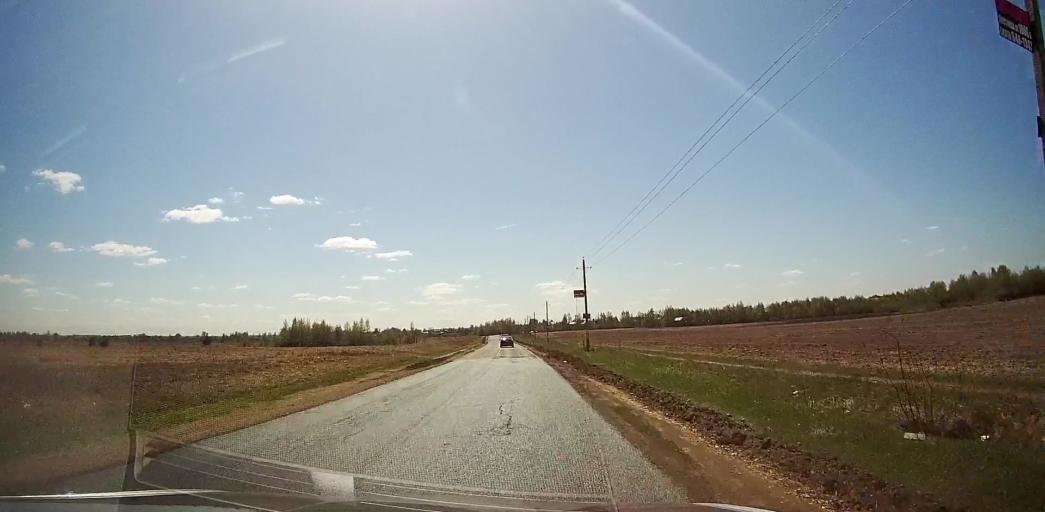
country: RU
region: Moskovskaya
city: Malyshevo
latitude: 55.4655
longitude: 38.3843
